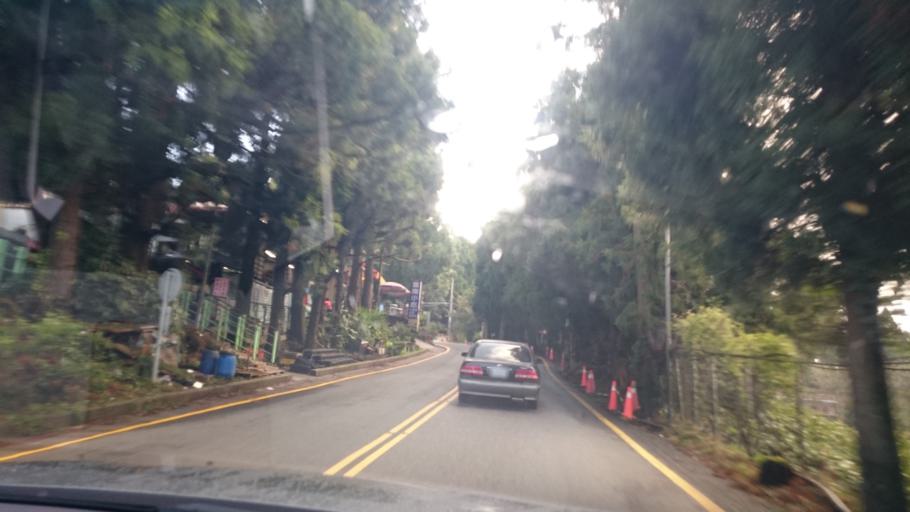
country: TW
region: Taiwan
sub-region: Nantou
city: Puli
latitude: 24.0474
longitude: 121.1564
